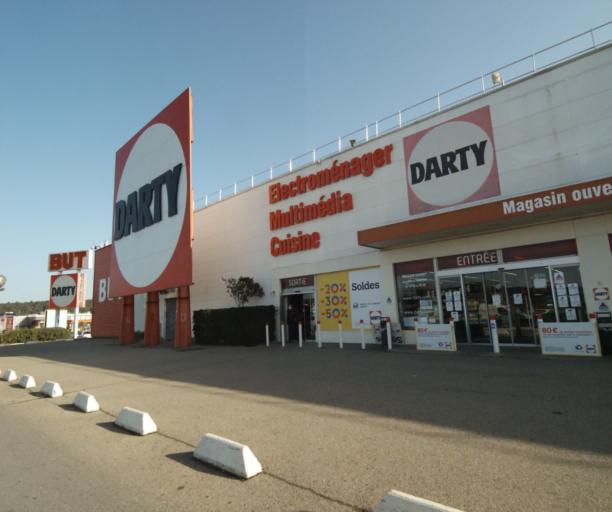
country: FR
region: Provence-Alpes-Cote d'Azur
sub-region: Departement des Bouches-du-Rhone
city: Septemes-les-Vallons
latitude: 43.4166
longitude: 5.3607
